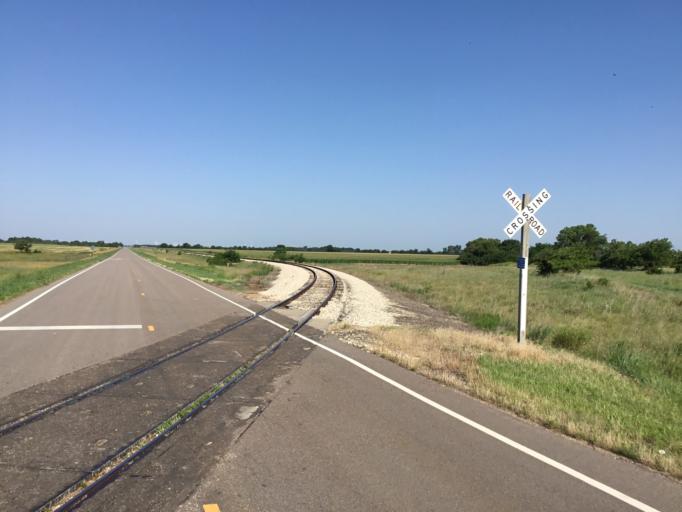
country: US
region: Kansas
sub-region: Kingman County
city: Kingman
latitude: 37.5460
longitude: -98.0334
